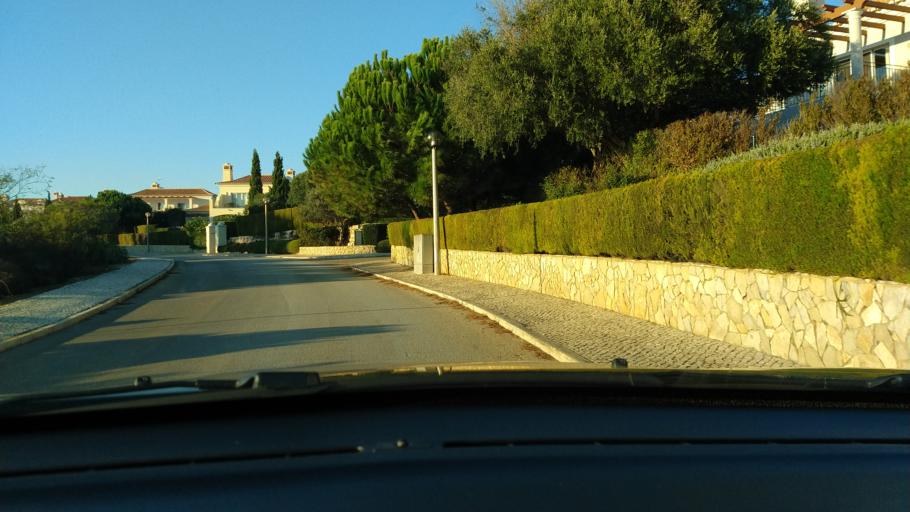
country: PT
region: Faro
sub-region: Vila do Bispo
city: Sagres
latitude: 37.0225
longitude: -8.9279
